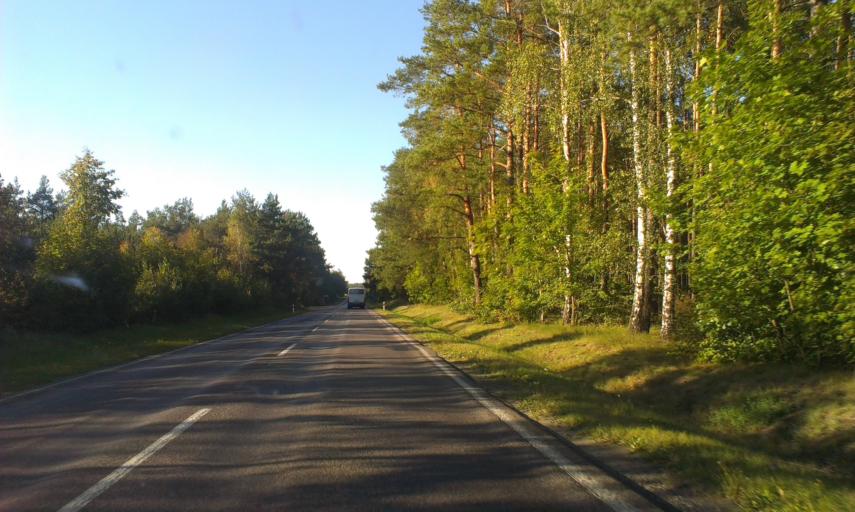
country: PL
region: Kujawsko-Pomorskie
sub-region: Powiat tucholski
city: Cekcyn
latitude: 53.5235
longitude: 17.9498
